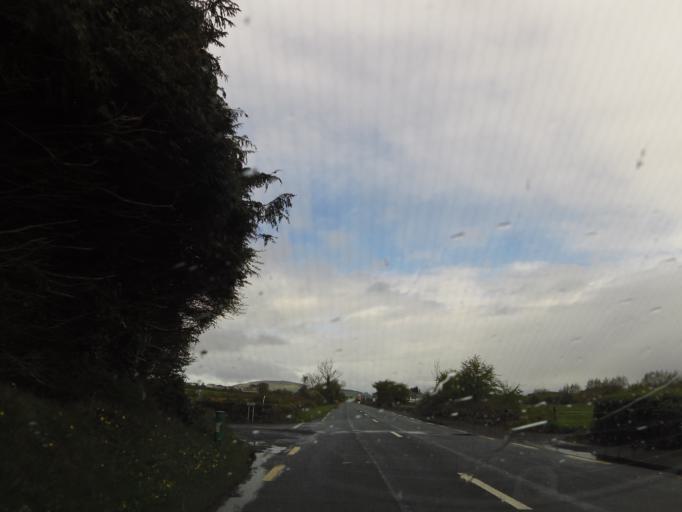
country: IE
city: Ballisodare
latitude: 54.1998
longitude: -8.4986
